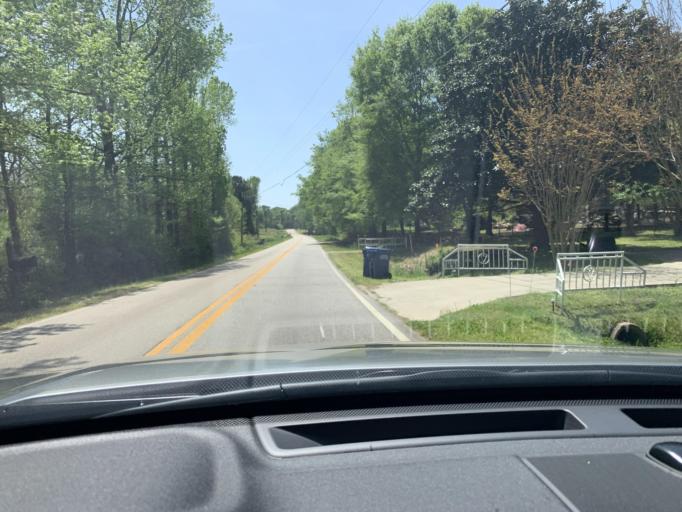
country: US
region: Georgia
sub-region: Barrow County
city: Statham
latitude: 33.8996
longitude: -83.6007
